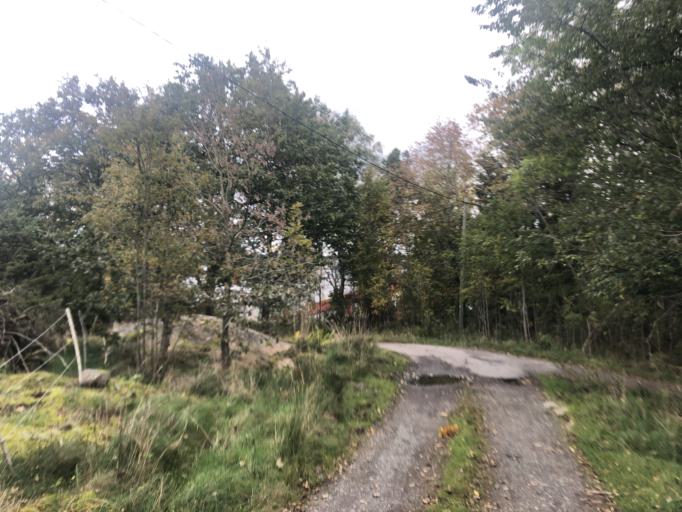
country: SE
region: Vaestra Goetaland
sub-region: Molndal
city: Moelndal
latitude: 57.6398
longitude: 11.9942
